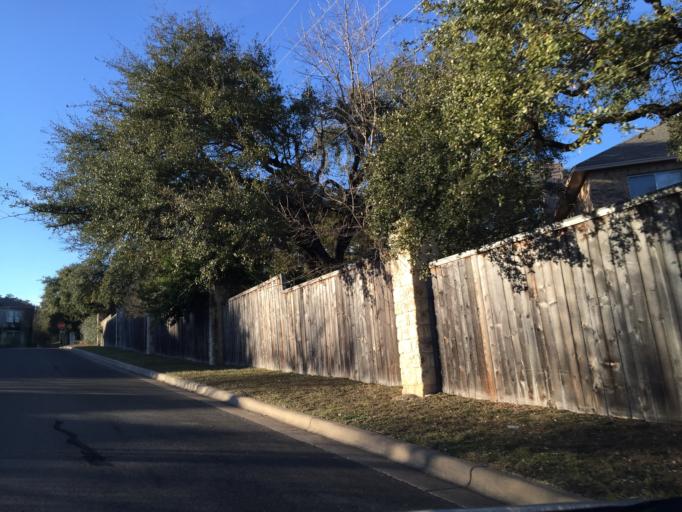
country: US
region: Texas
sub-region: Travis County
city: Rollingwood
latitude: 30.2724
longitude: -97.8195
